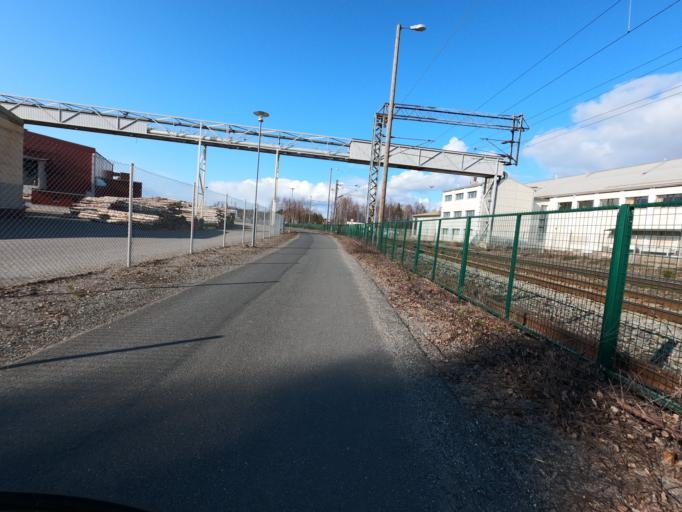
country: FI
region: North Karelia
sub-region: Joensuu
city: Joensuu
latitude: 62.6037
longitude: 29.7802
